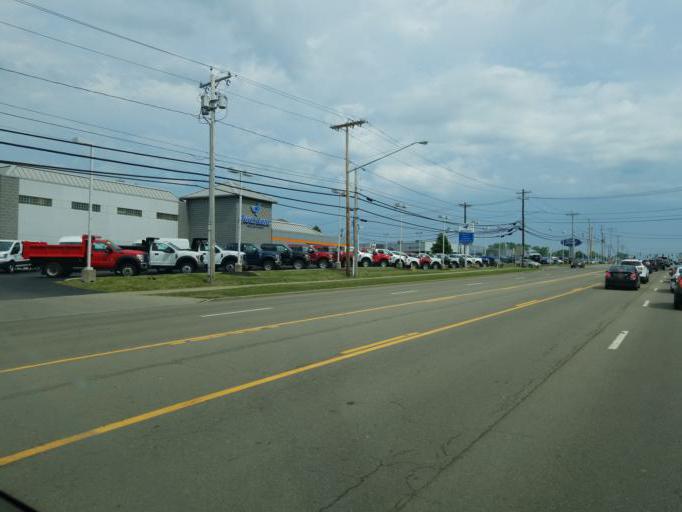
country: US
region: New York
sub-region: Erie County
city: Hamburg
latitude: 42.7520
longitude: -78.8564
